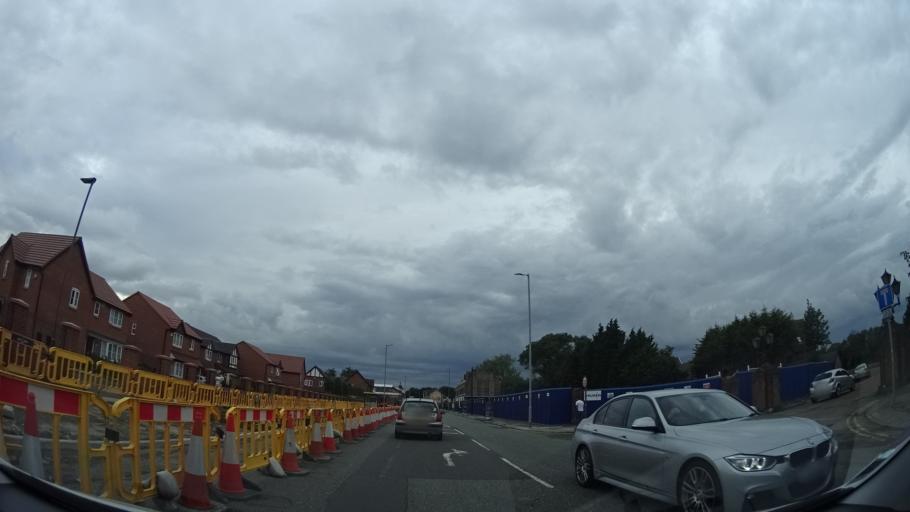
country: GB
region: England
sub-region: Liverpool
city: Liverpool
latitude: 53.4144
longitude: -2.9302
